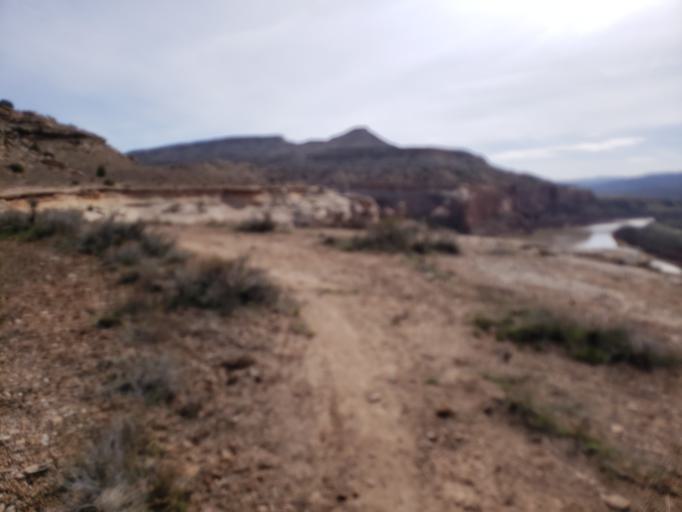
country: US
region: Colorado
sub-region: Mesa County
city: Loma
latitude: 39.1910
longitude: -108.8825
